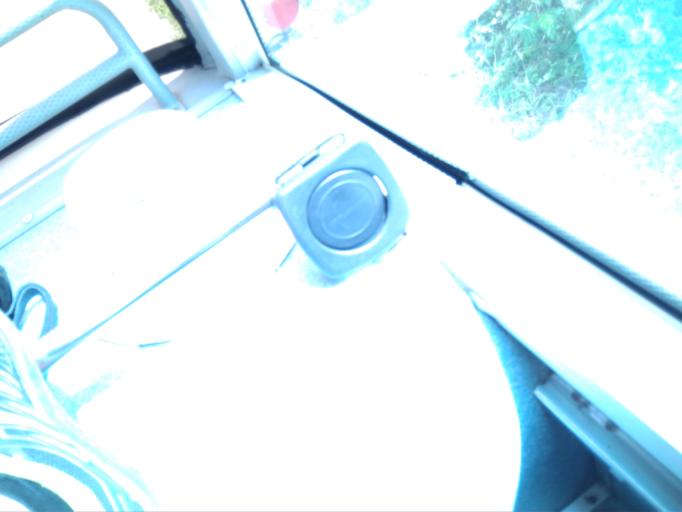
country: TH
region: Krabi
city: Plai Phraya
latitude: 8.4271
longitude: 98.8310
